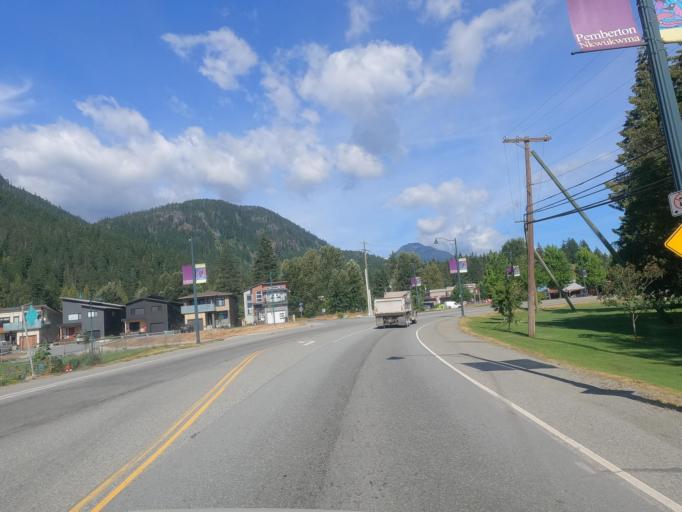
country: CA
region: British Columbia
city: Pemberton
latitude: 50.3199
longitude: -122.8046
